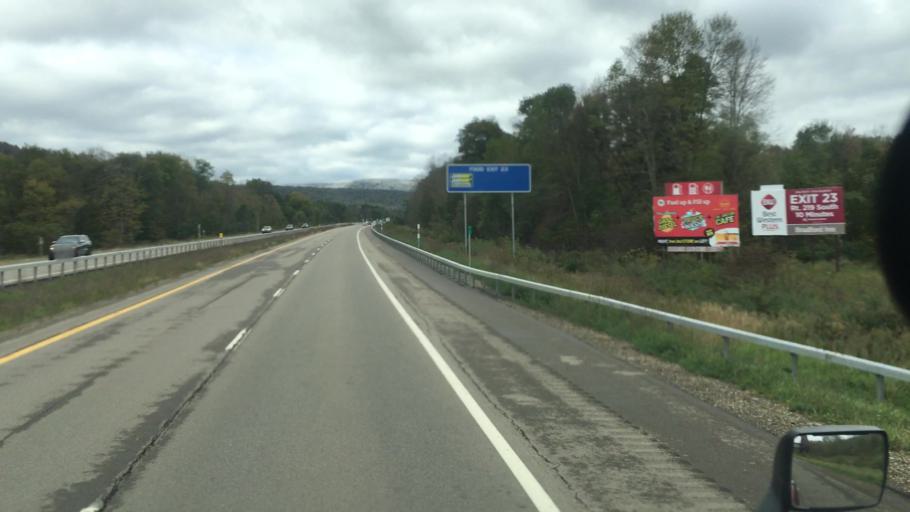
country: US
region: Pennsylvania
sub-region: McKean County
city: Foster Brook
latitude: 42.0858
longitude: -78.6116
